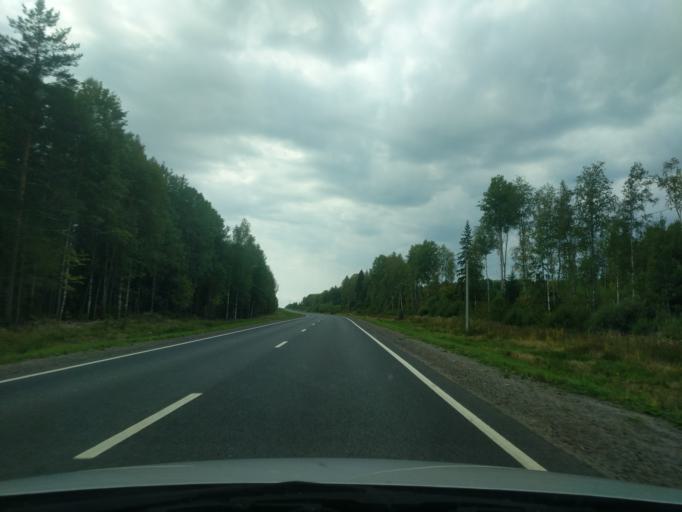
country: RU
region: Kostroma
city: Manturovo
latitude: 58.1546
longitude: 44.3811
